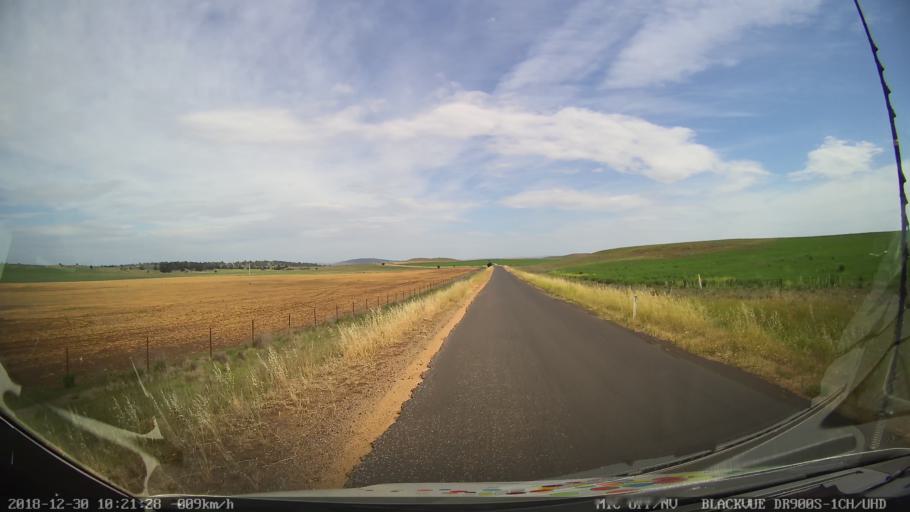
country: AU
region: New South Wales
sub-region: Snowy River
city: Berridale
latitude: -36.5511
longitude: 149.0038
